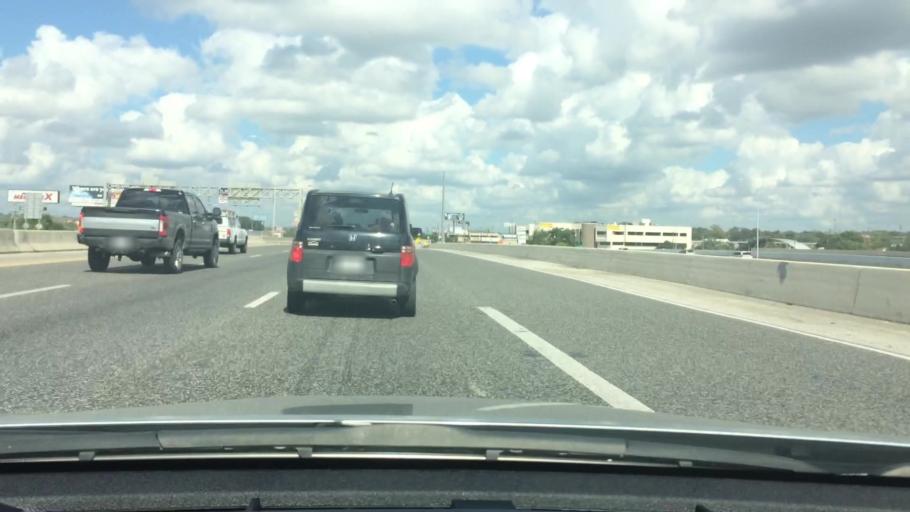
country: US
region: Texas
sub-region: Bexar County
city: Windcrest
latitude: 29.5225
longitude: -98.3947
